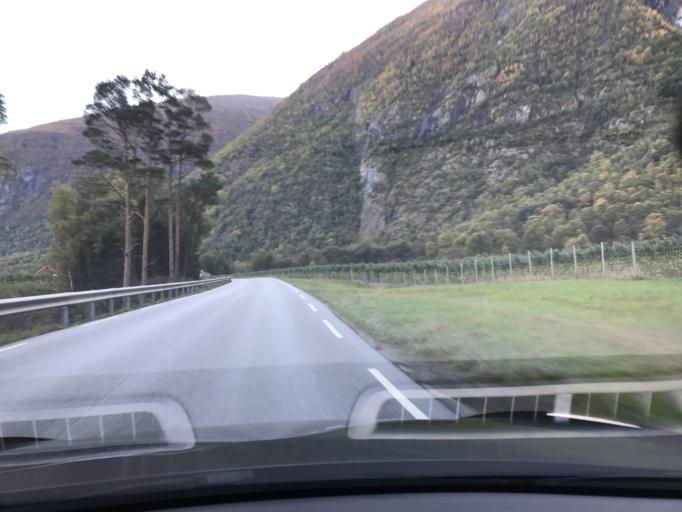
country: NO
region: Sogn og Fjordane
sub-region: Laerdal
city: Laerdalsoyri
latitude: 61.0746
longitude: 7.5010
